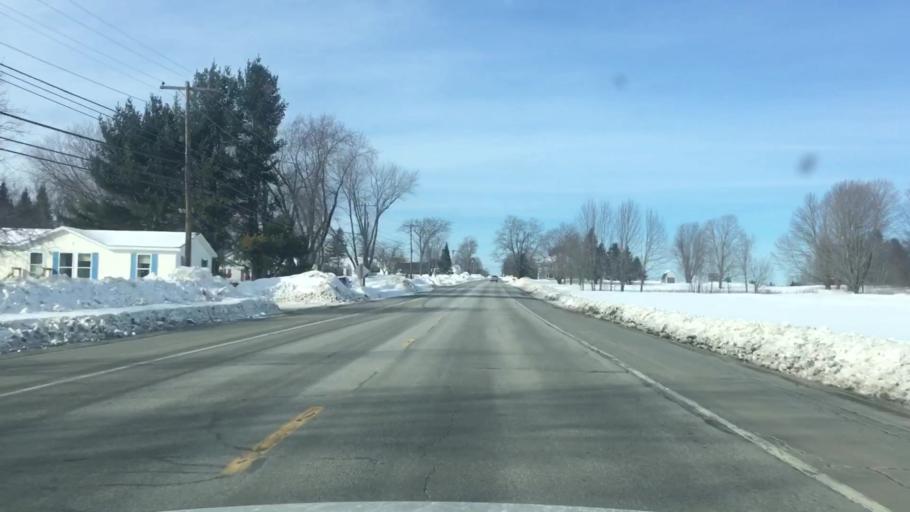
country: US
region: Maine
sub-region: Penobscot County
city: Charleston
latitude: 45.0213
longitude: -69.0291
